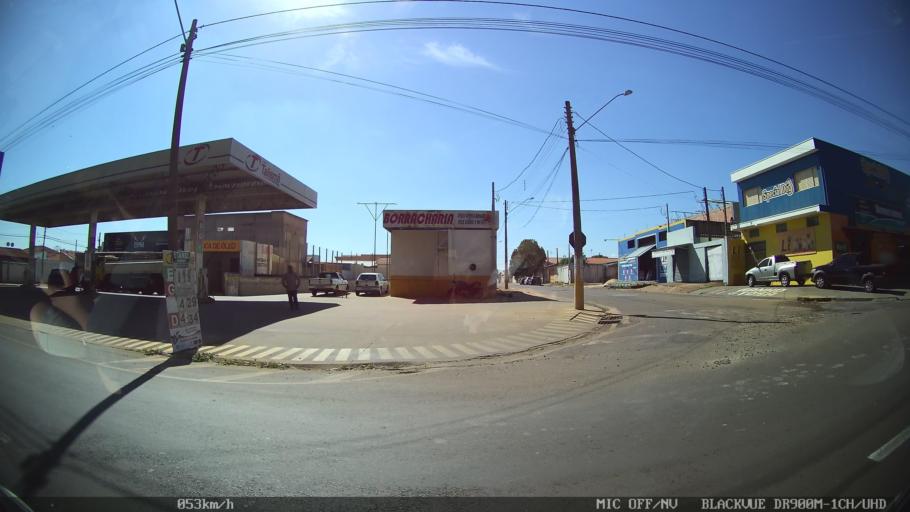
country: BR
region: Sao Paulo
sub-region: Franca
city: Franca
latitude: -20.5455
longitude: -47.4528
